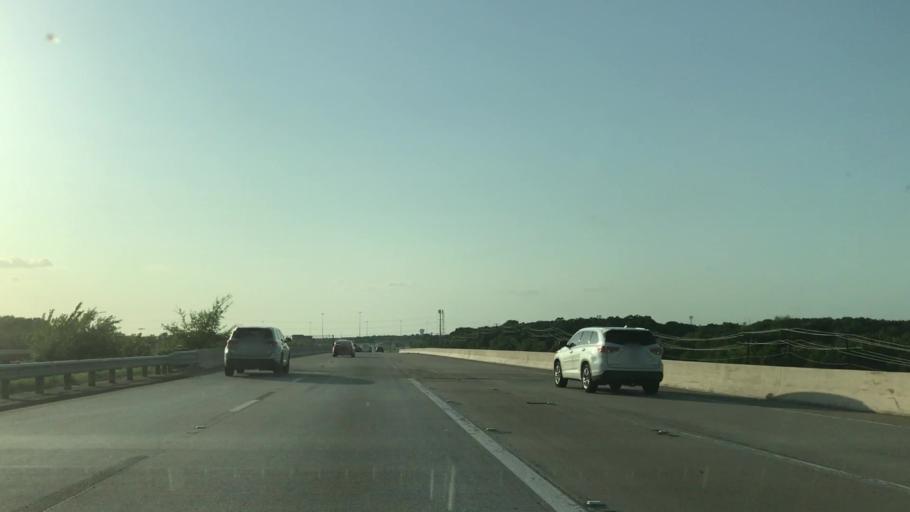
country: US
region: Texas
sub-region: Tarrant County
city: Grapevine
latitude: 32.8952
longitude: -97.0859
